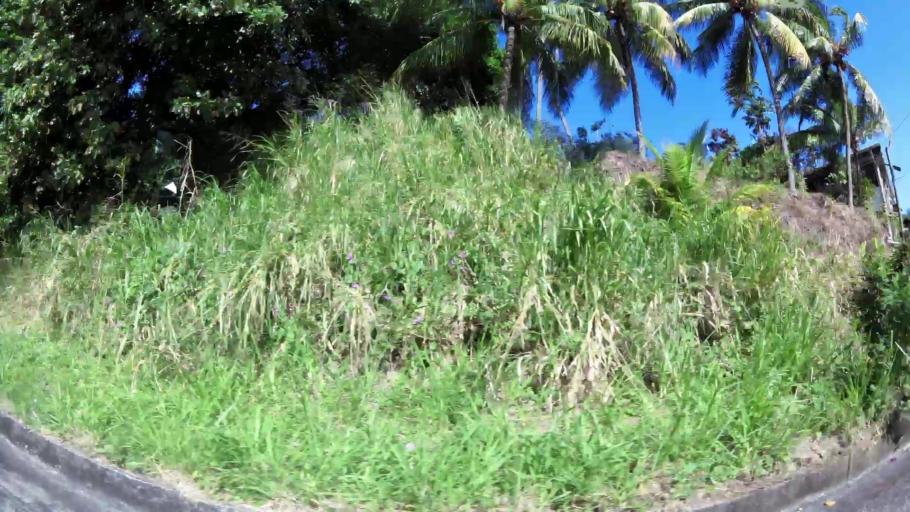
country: MQ
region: Martinique
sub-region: Martinique
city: Le Lorrain
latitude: 14.8365
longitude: -61.0680
